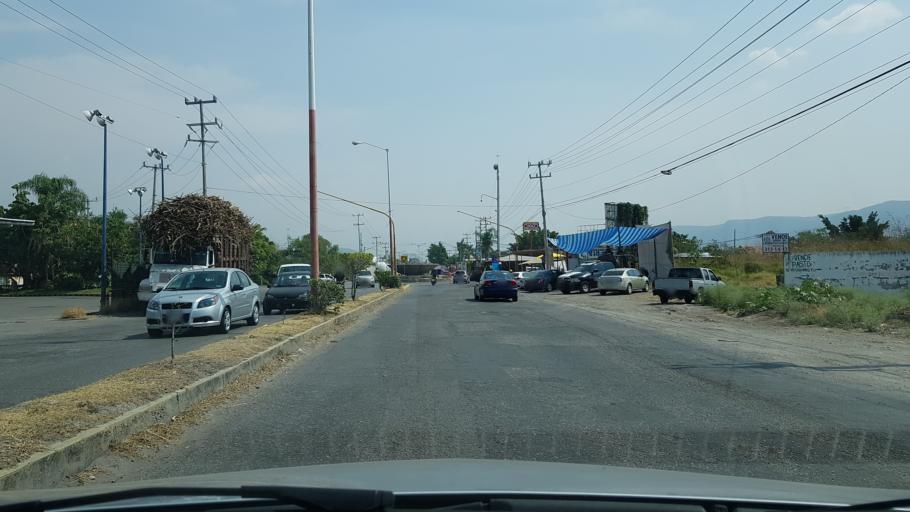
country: MX
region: Morelos
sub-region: Xochitepec
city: Chiconcuac
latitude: 18.7957
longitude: -99.2007
